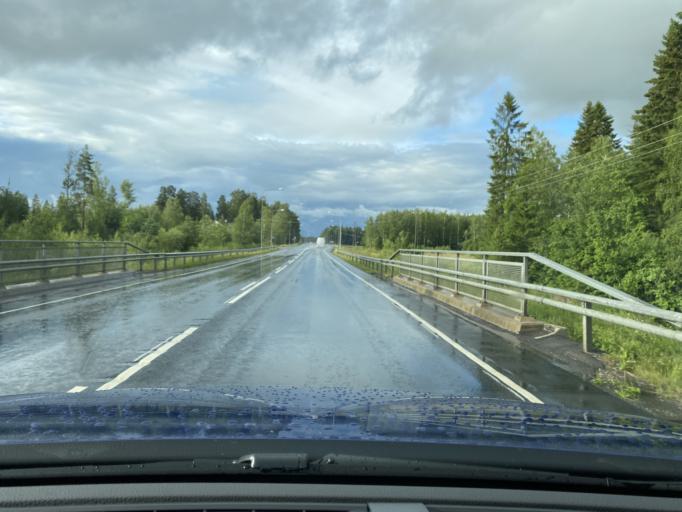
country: FI
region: Uusimaa
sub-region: Helsinki
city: Nurmijaervi
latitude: 60.4692
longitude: 24.8389
